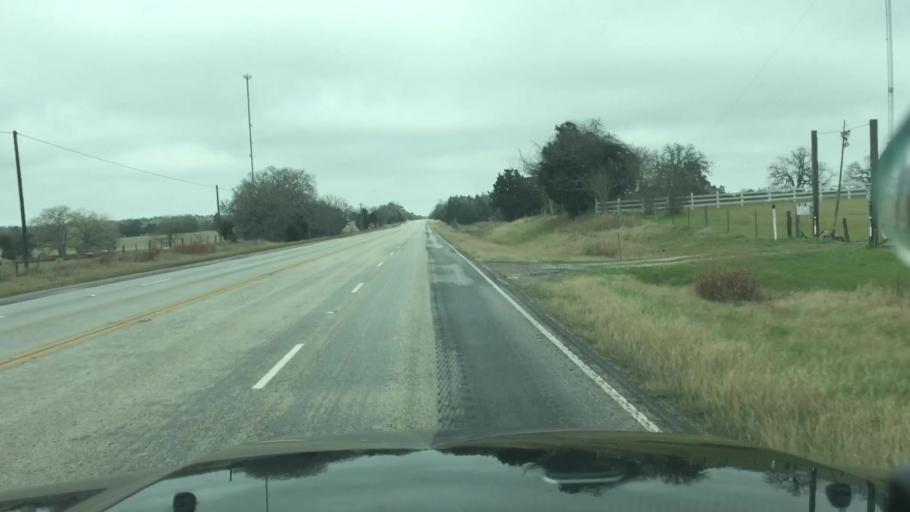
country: US
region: Texas
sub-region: Lee County
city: Giddings
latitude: 30.1043
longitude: -96.9142
